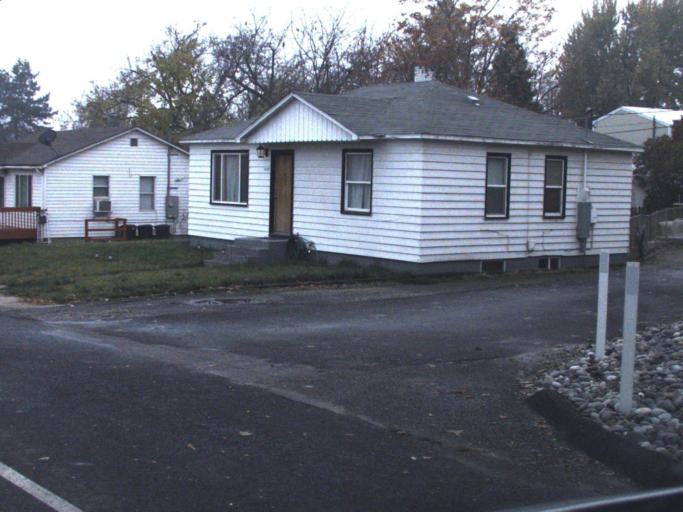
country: US
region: Washington
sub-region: Asotin County
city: Clarkston
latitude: 46.4004
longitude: -117.0443
